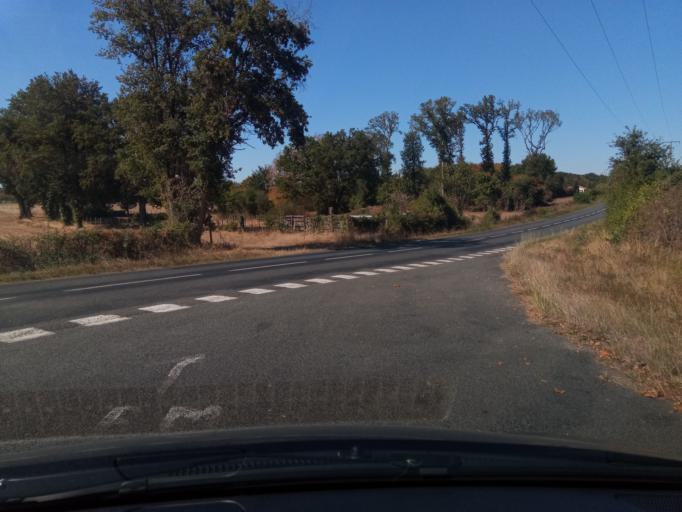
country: FR
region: Poitou-Charentes
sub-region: Departement de la Vienne
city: Montmorillon
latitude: 46.4830
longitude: 0.8477
